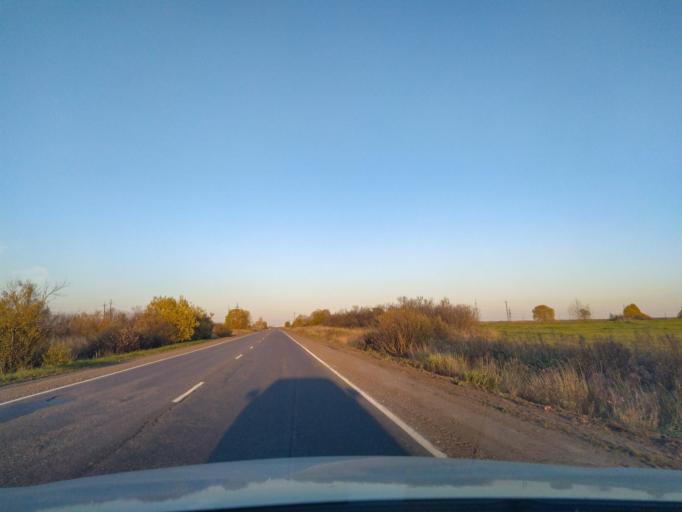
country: RU
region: Leningrad
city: Kobrinskoye
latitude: 59.4784
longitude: 30.1401
